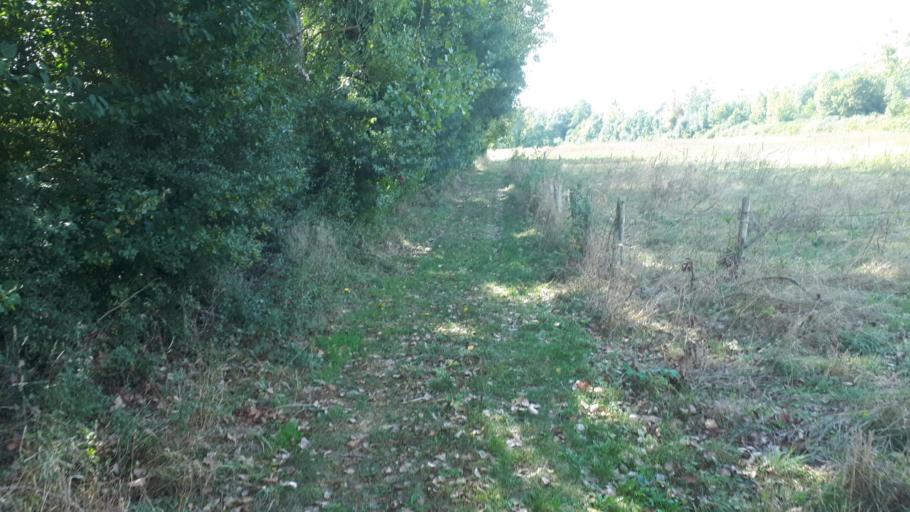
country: FR
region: Centre
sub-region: Departement du Loir-et-Cher
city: Villiers-sur-Loir
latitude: 47.8184
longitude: 0.9631
